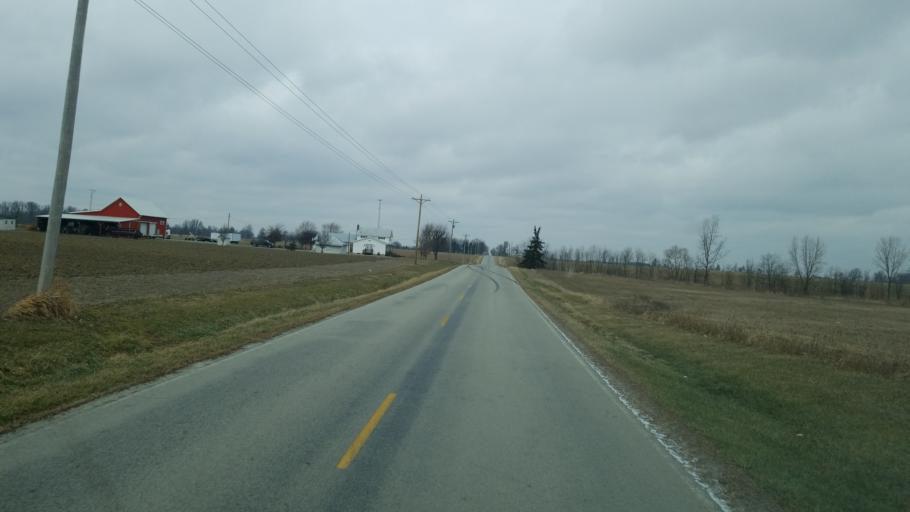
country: US
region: Ohio
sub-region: Hardin County
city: Forest
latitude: 40.7836
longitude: -83.4195
